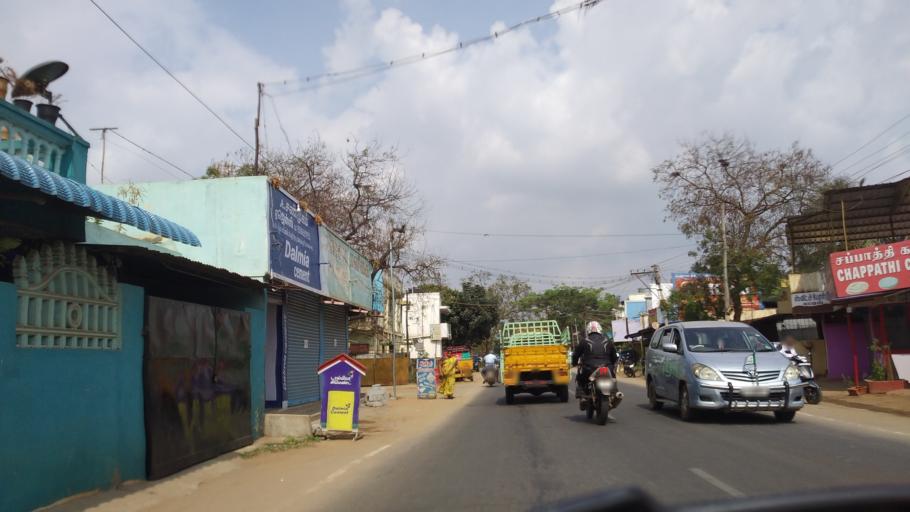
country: IN
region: Tamil Nadu
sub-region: Coimbatore
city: Perur
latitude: 10.9482
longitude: 76.9355
